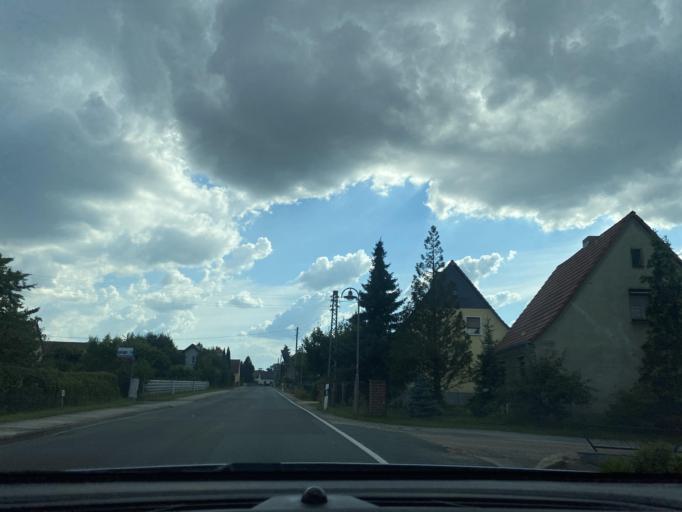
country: DE
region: Saxony
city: Klitten
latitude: 51.3523
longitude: 14.6057
